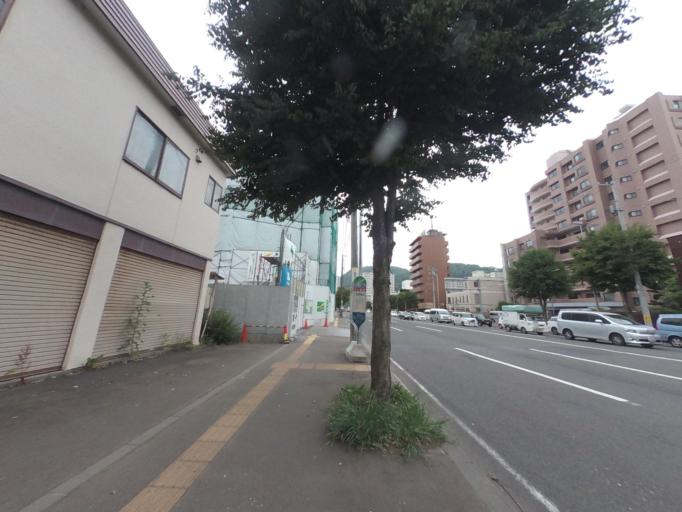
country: JP
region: Hokkaido
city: Sapporo
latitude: 43.0575
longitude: 141.3157
